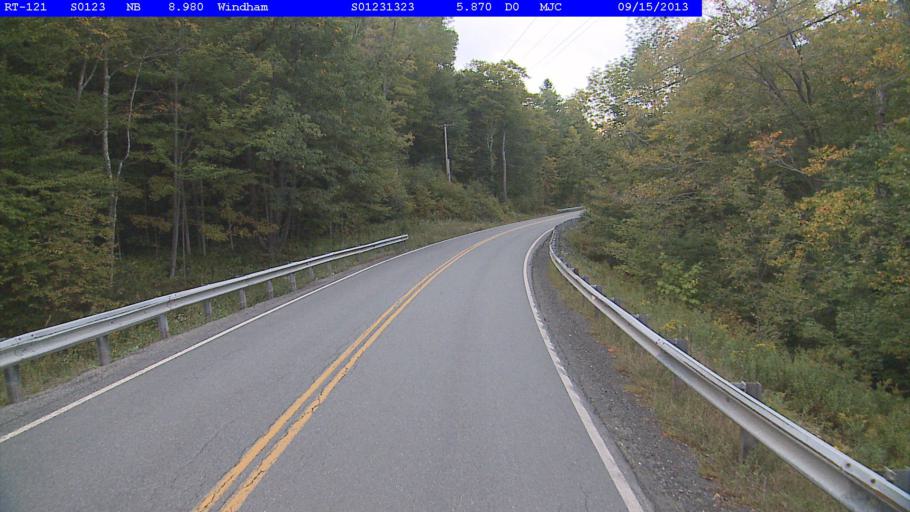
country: US
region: Vermont
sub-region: Windsor County
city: Chester
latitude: 43.2008
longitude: -72.7319
